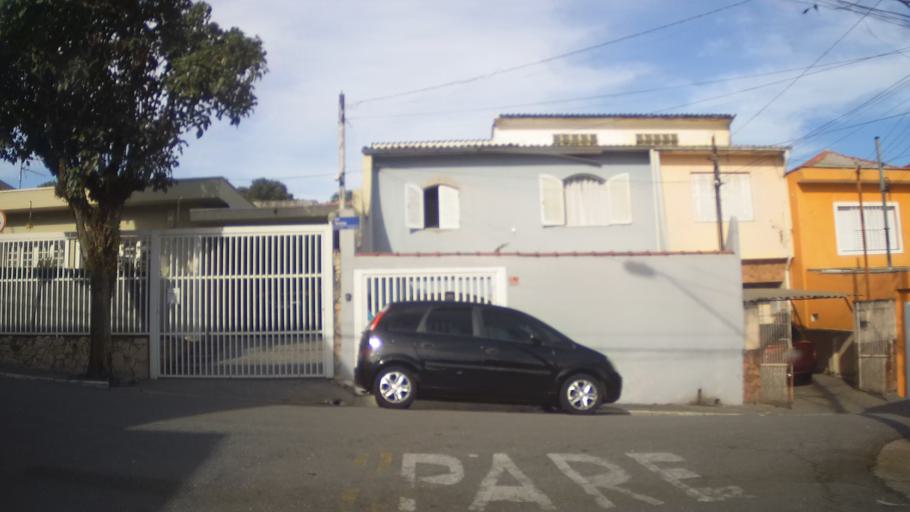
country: BR
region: Sao Paulo
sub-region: Sao Caetano Do Sul
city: Sao Caetano do Sul
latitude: -23.6284
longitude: -46.5751
